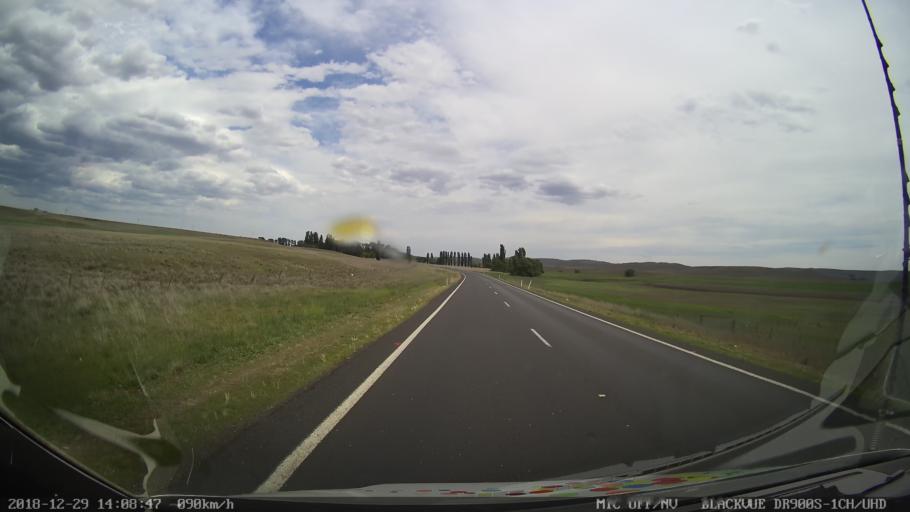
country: AU
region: New South Wales
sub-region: Cooma-Monaro
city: Cooma
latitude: -36.3699
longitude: 149.2135
